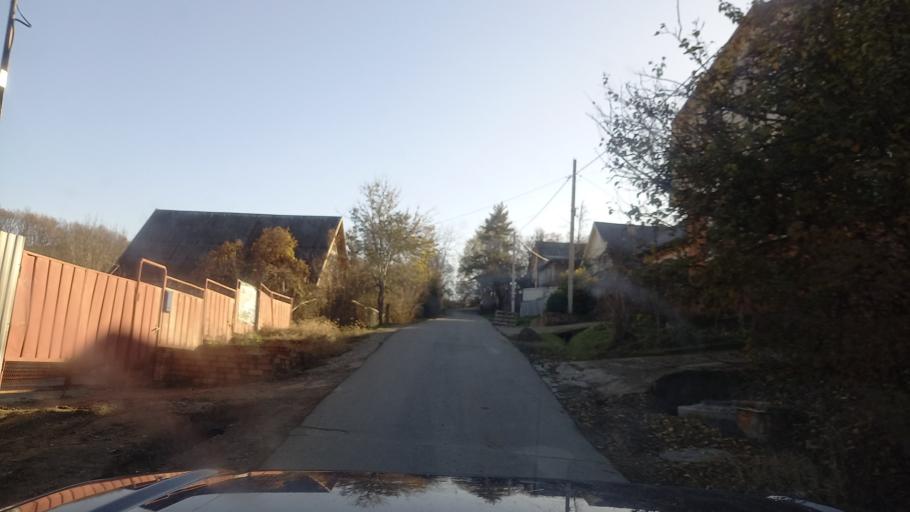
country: RU
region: Krasnodarskiy
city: Goryachiy Klyuch
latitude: 44.6238
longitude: 39.1065
